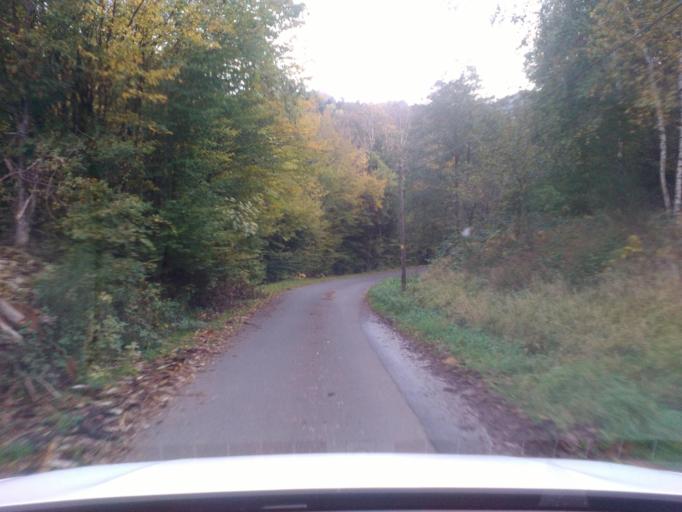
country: FR
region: Lorraine
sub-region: Departement des Vosges
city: Senones
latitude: 48.4183
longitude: 7.0664
